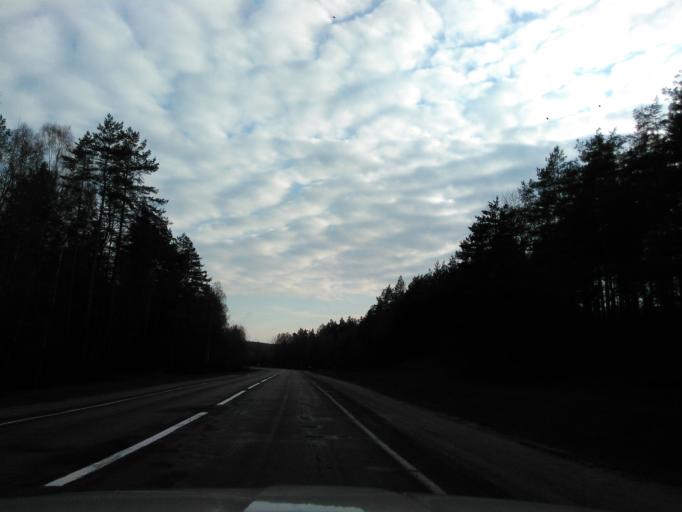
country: BY
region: Minsk
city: Plyeshchanitsy
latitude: 54.3529
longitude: 27.8822
